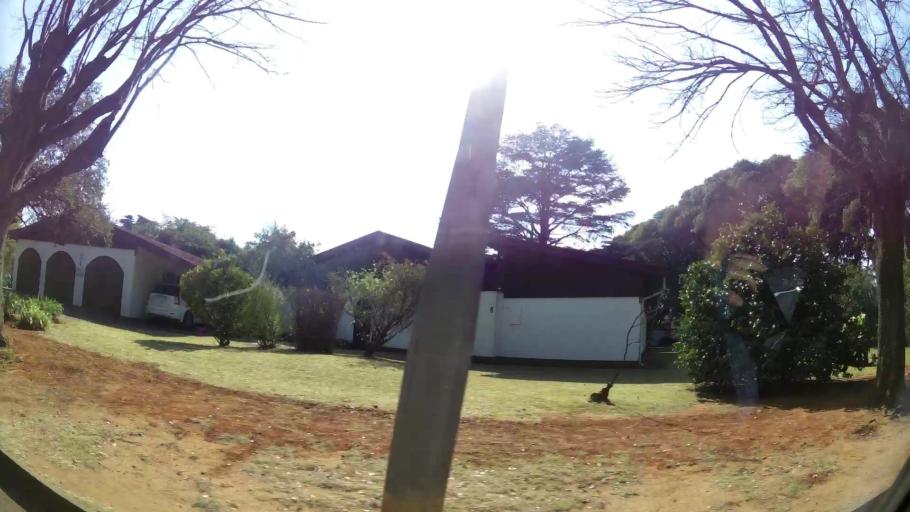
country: ZA
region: Gauteng
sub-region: Ekurhuleni Metropolitan Municipality
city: Benoni
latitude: -26.1849
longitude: 28.2858
